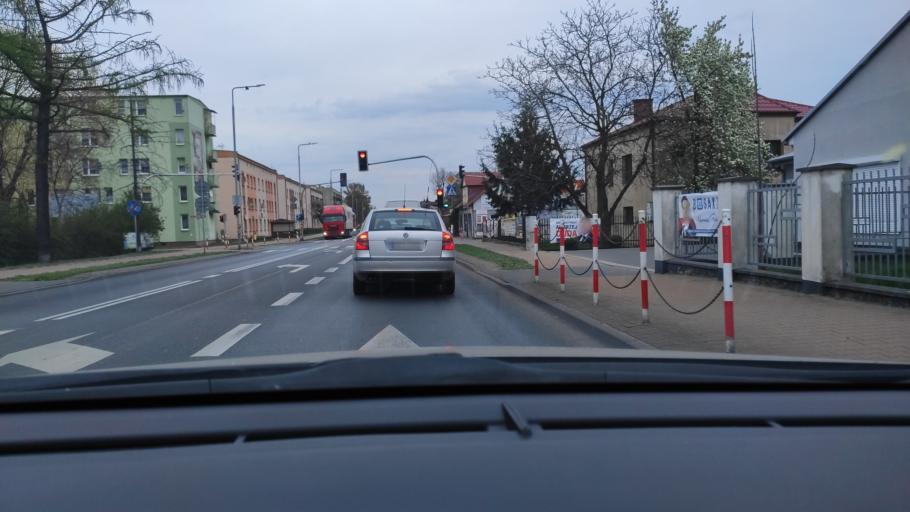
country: PL
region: Masovian Voivodeship
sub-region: Powiat zwolenski
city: Zwolen
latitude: 51.3578
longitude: 21.5748
